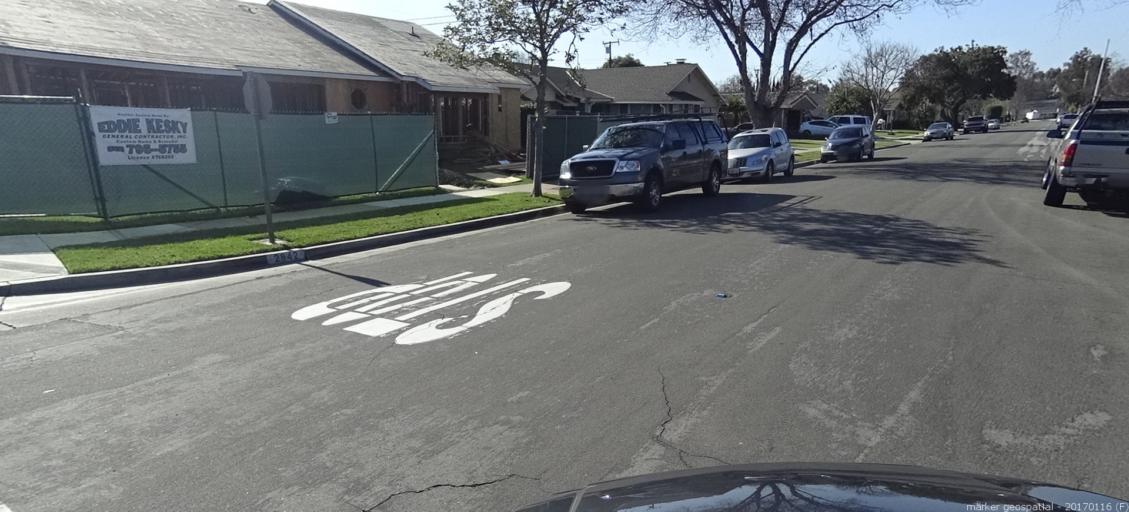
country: US
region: California
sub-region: Orange County
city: Rossmoor
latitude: 33.7786
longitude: -118.0844
